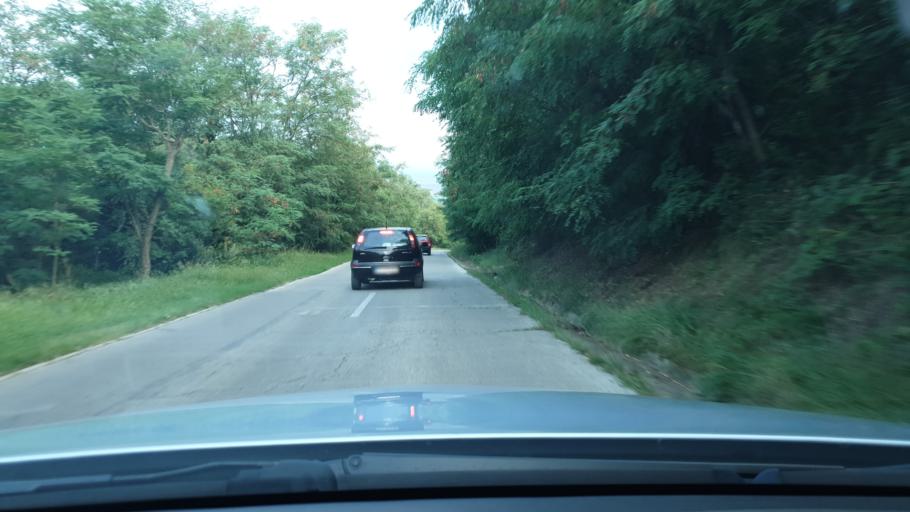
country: RS
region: Autonomna Pokrajina Vojvodina
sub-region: Juznobanatski Okrug
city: Vrsac
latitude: 45.1220
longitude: 21.3291
